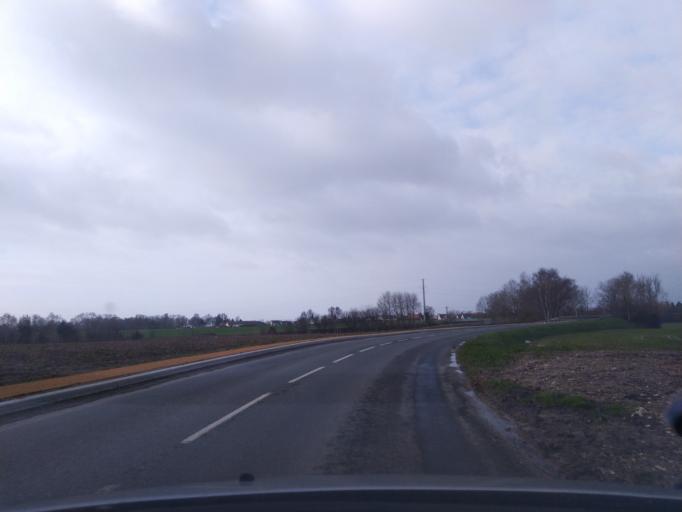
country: FR
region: Haute-Normandie
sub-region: Departement de la Seine-Maritime
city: Roumare
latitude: 49.5150
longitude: 0.9864
